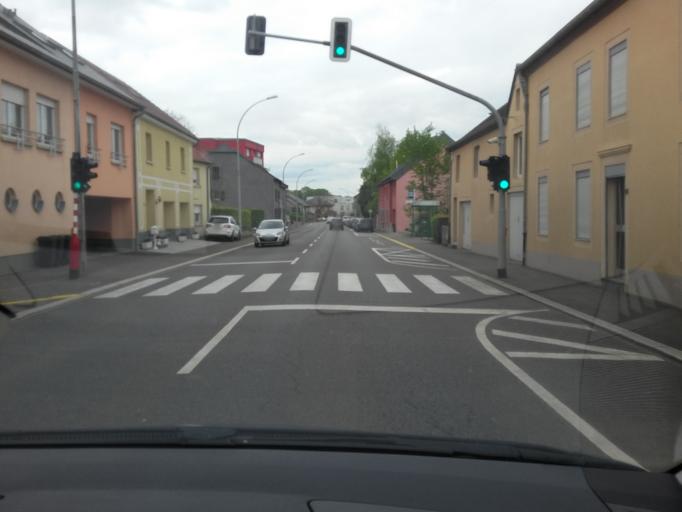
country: LU
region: Luxembourg
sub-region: Canton de Capellen
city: Dippach
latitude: 49.5878
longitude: 5.9803
